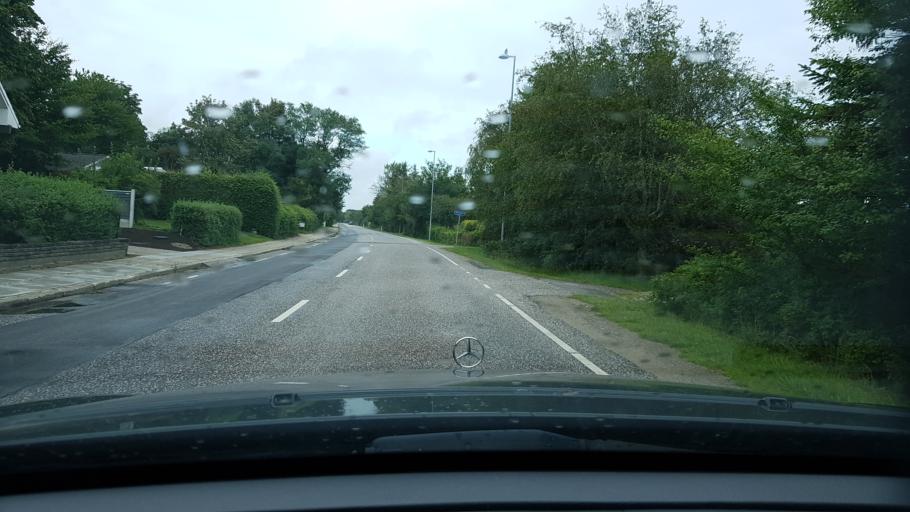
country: DK
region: North Denmark
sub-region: Mariagerfjord Kommune
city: Hadsund
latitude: 56.8110
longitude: 10.2708
